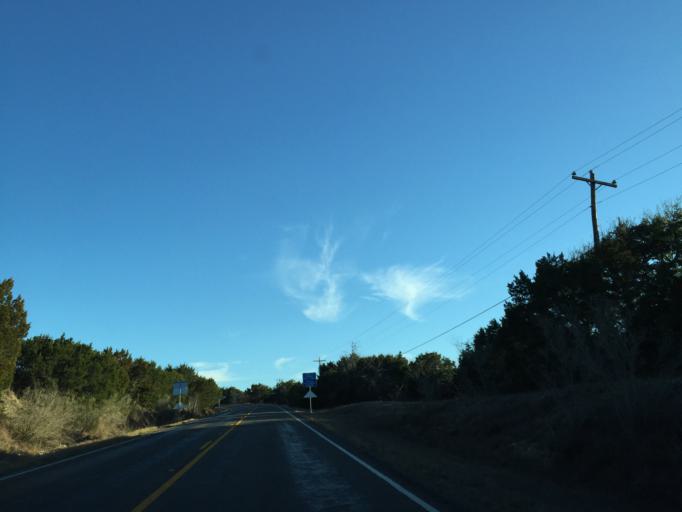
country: US
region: Texas
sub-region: Travis County
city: Lago Vista
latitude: 30.5135
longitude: -98.0413
